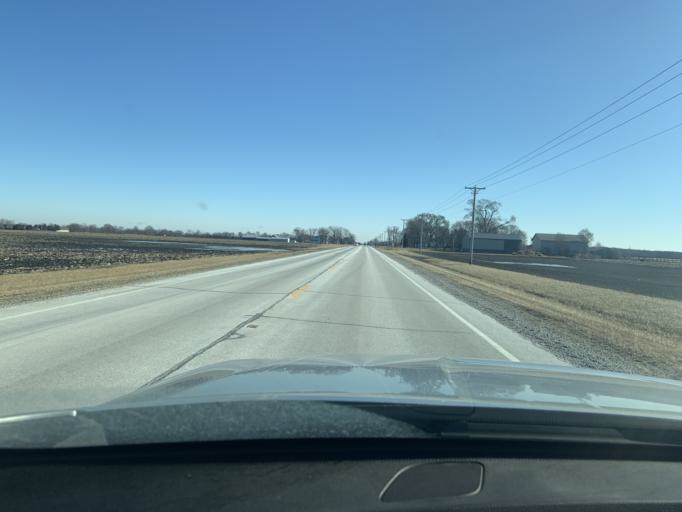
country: US
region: Illinois
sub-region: LaSalle County
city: Seneca
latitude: 41.3704
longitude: -88.5264
